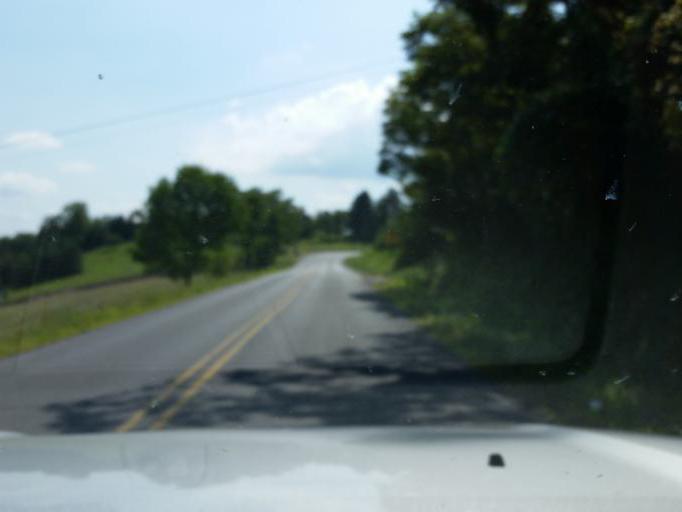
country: US
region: Pennsylvania
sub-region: Blair County
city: Duncansville
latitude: 40.4307
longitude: -78.4513
